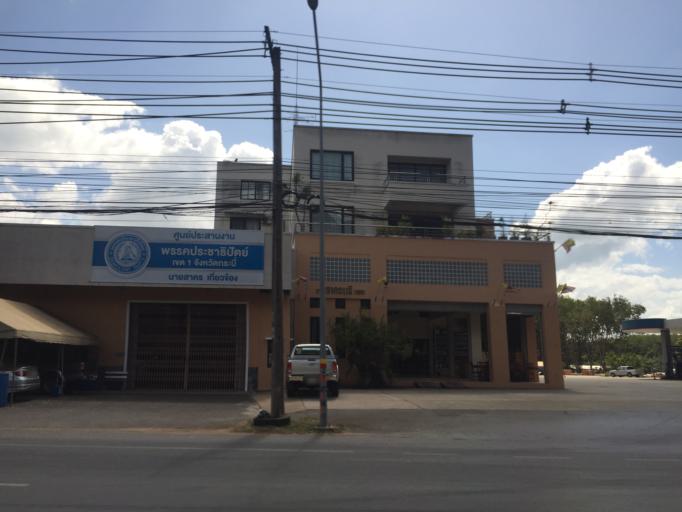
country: TH
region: Krabi
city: Krabi
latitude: 8.0802
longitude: 98.8568
